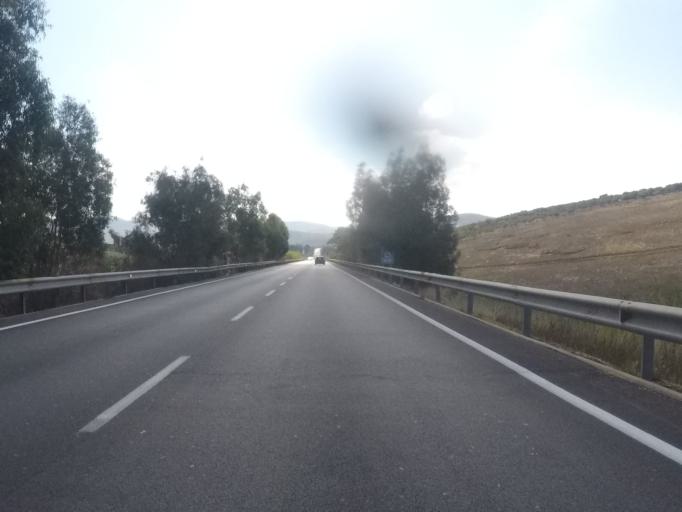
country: IT
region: Sicily
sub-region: Agrigento
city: Ribera
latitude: 37.4315
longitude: 13.2907
